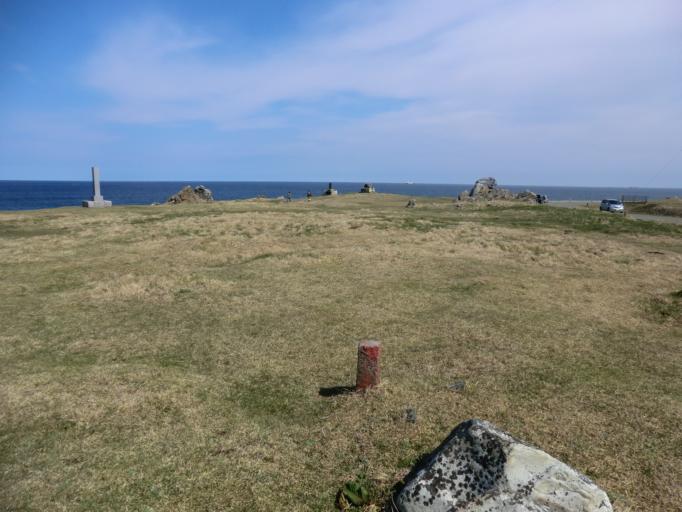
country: JP
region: Aomori
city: Mutsu
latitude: 41.4295
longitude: 141.4620
